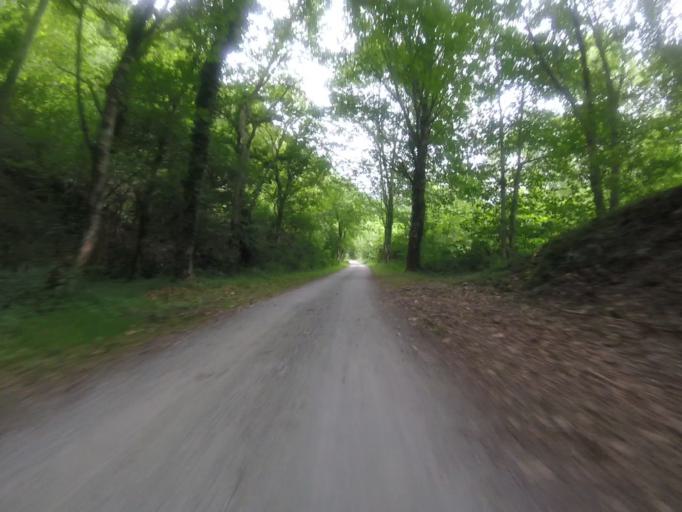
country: ES
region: Navarre
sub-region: Provincia de Navarra
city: Sunbilla
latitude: 43.2021
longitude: -1.6728
